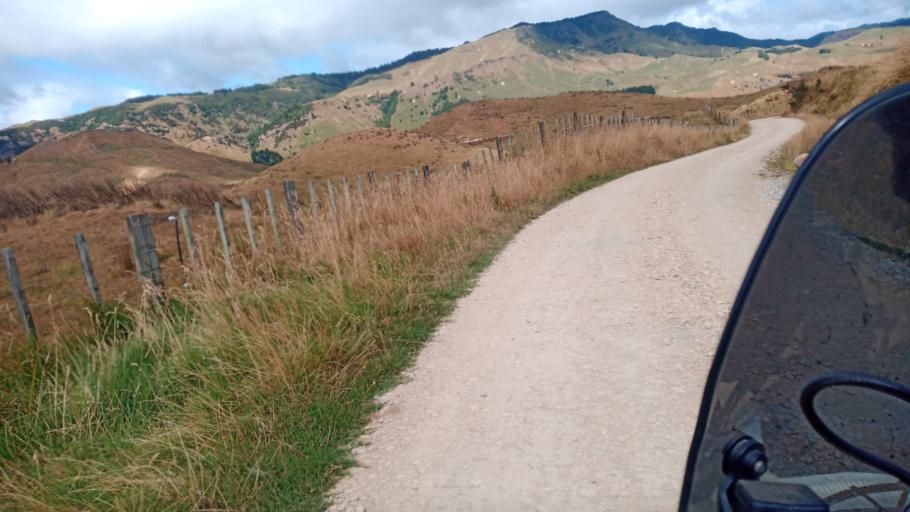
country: NZ
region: Hawke's Bay
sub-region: Wairoa District
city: Wairoa
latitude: -38.6117
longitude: 177.4358
